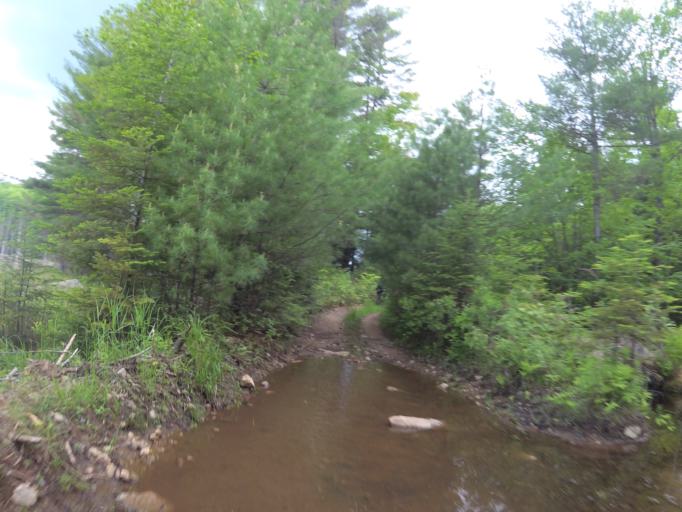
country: CA
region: Ontario
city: Renfrew
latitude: 45.0608
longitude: -76.8881
